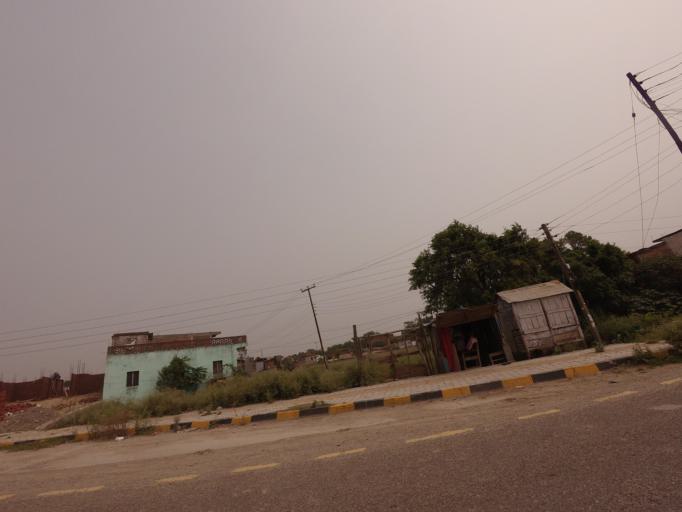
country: IN
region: Uttar Pradesh
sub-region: Maharajganj
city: Nautanwa
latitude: 27.5025
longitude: 83.3424
